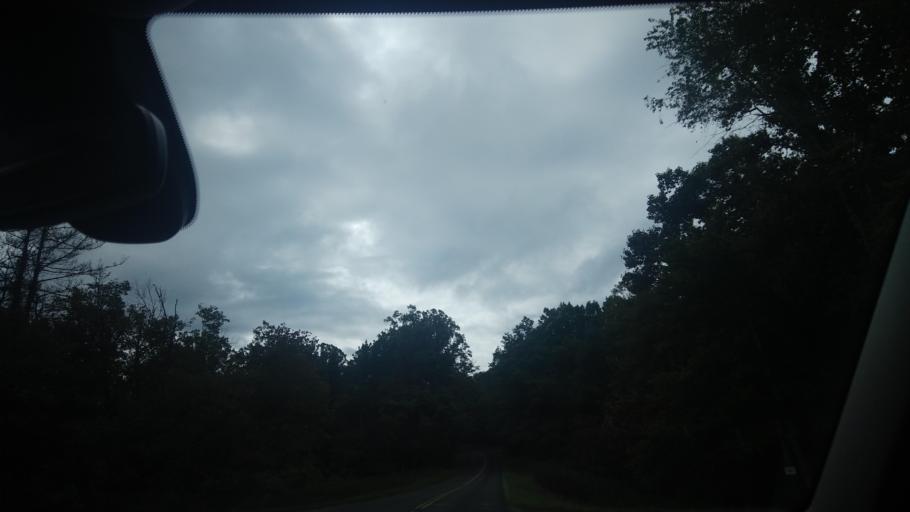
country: US
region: Virginia
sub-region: Carroll County
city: Cana
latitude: 36.6522
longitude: -80.5523
